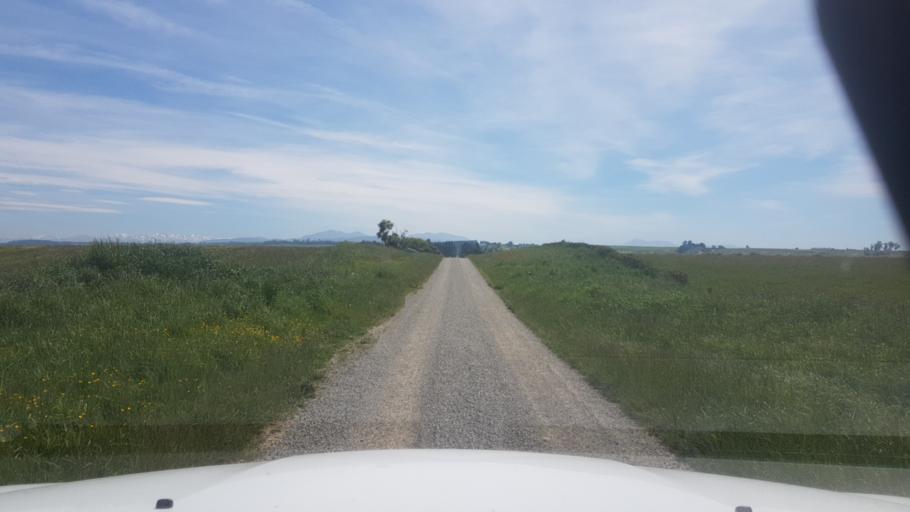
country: NZ
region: Canterbury
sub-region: Timaru District
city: Pleasant Point
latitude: -44.2288
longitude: 171.1656
